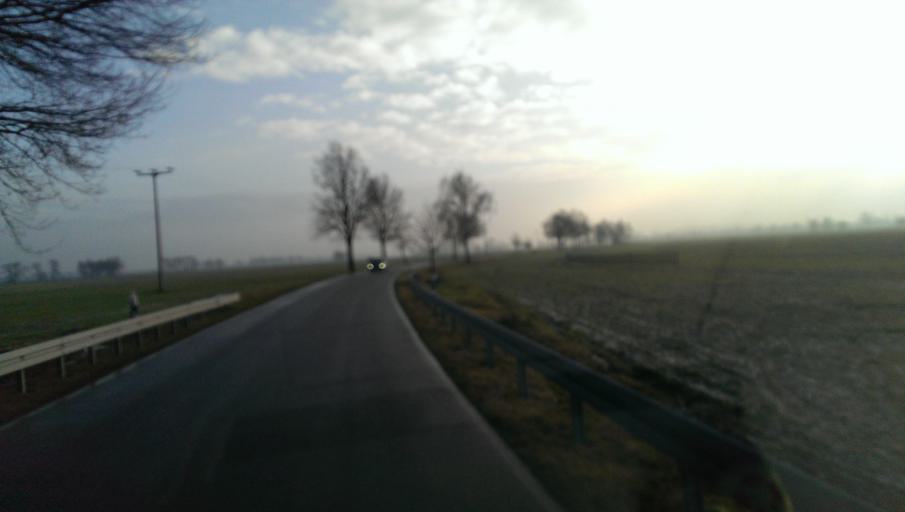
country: DE
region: Brandenburg
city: Bad Liebenwerda
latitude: 51.4733
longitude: 13.4240
